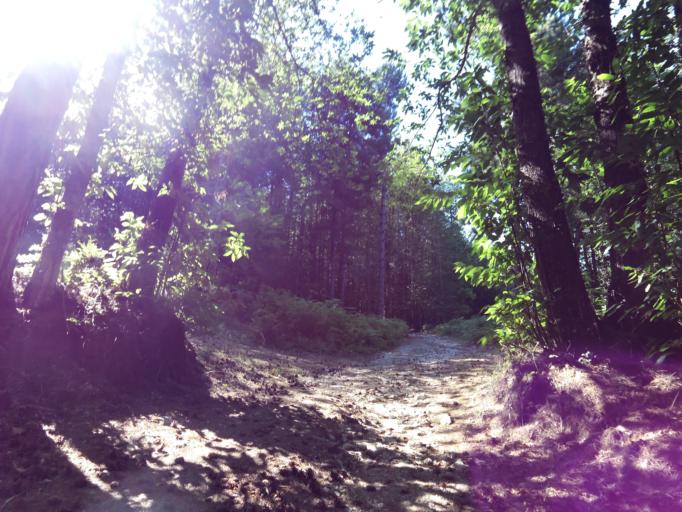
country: IT
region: Calabria
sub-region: Provincia di Vibo-Valentia
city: Nardodipace
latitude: 38.4975
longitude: 16.3847
